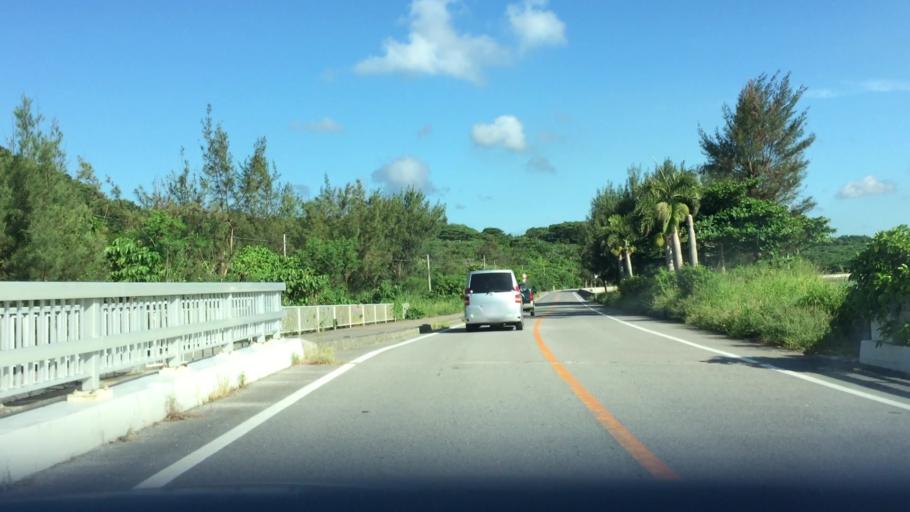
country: JP
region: Okinawa
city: Ishigaki
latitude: 24.4332
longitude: 124.1236
